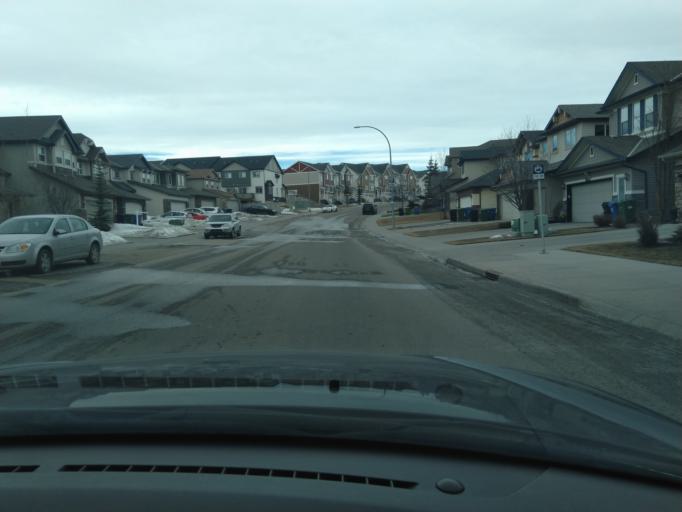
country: CA
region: Alberta
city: Calgary
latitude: 51.1630
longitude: -114.0932
